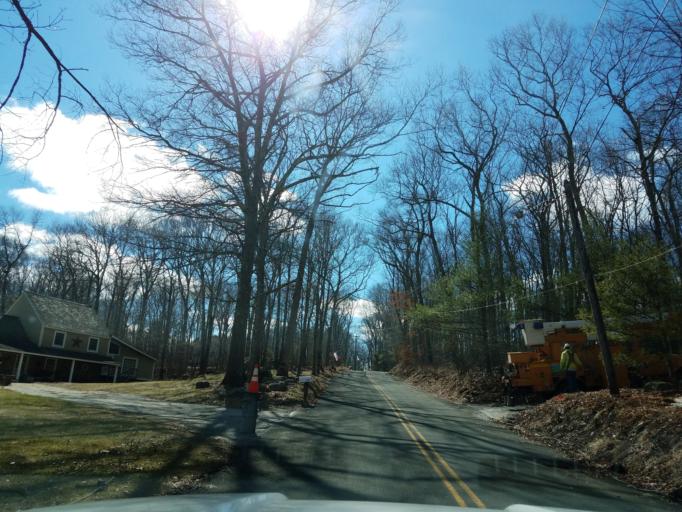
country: US
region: Connecticut
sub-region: Windham County
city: North Grosvenor Dale
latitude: 42.0002
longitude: -71.8810
